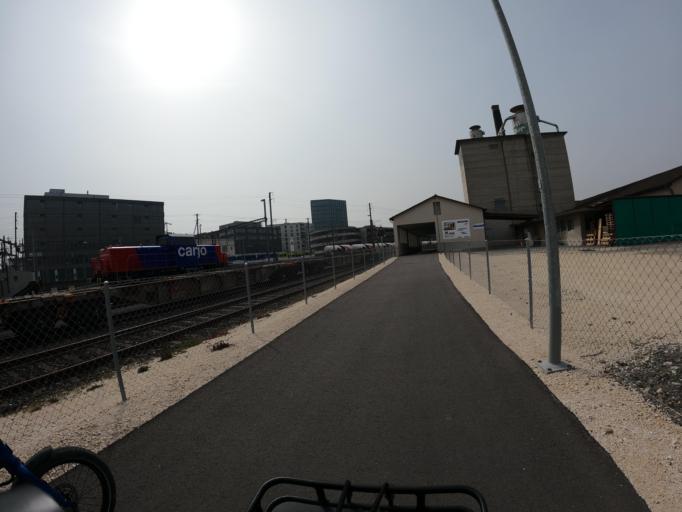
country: CH
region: Aargau
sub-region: Bezirk Aarau
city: Aarau
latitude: 47.3940
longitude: 8.0602
